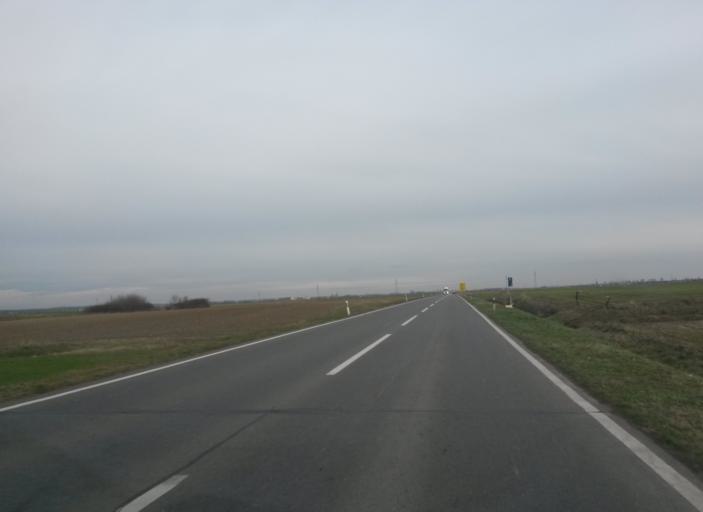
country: HR
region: Osjecko-Baranjska
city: Cepin
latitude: 45.5401
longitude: 18.5868
